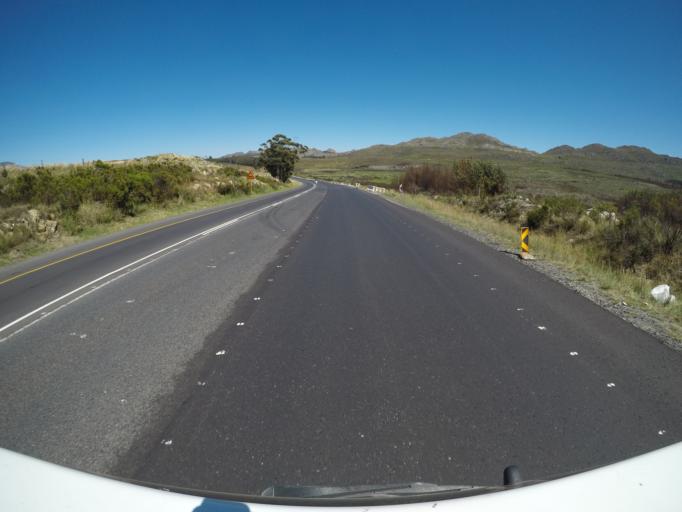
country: ZA
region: Western Cape
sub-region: Overberg District Municipality
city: Grabouw
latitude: -34.1515
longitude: 18.9562
